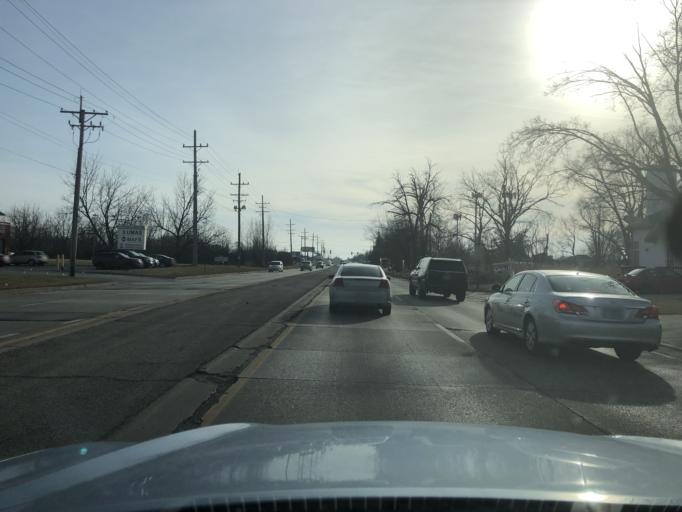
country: US
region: Illinois
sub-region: DuPage County
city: Roselle
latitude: 42.0011
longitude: -88.0802
